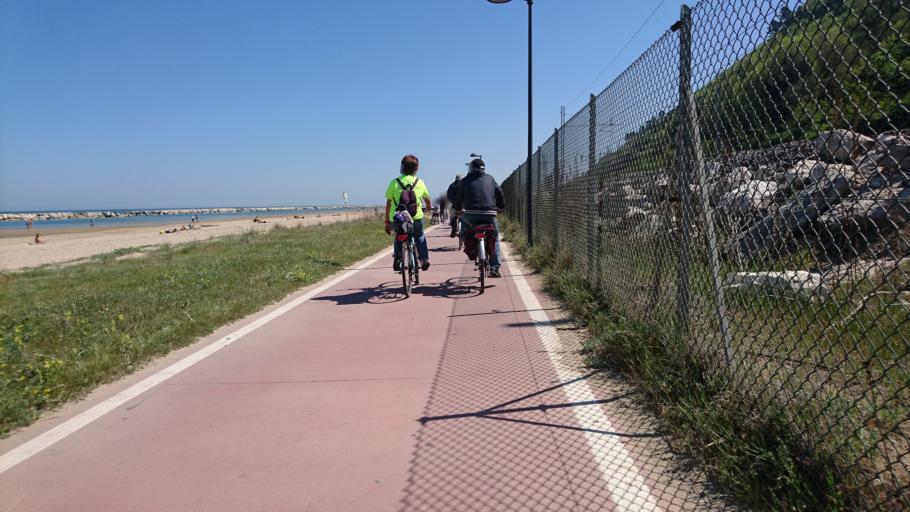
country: IT
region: The Marches
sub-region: Provincia di Pesaro e Urbino
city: Pesaro
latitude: 43.8994
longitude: 12.9387
